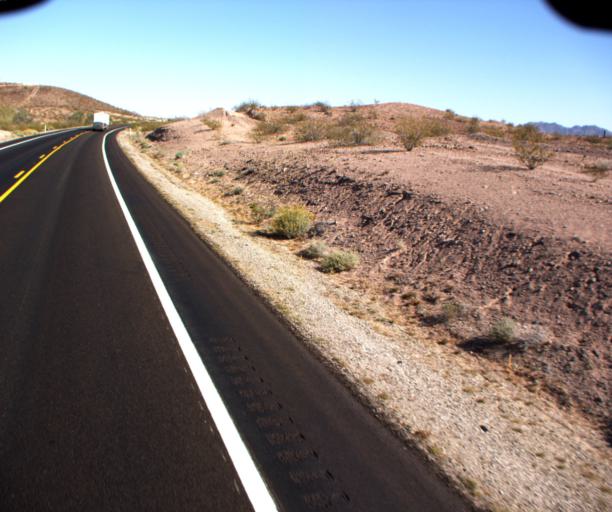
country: US
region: Arizona
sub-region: Yuma County
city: Wellton
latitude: 33.0977
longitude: -114.2981
